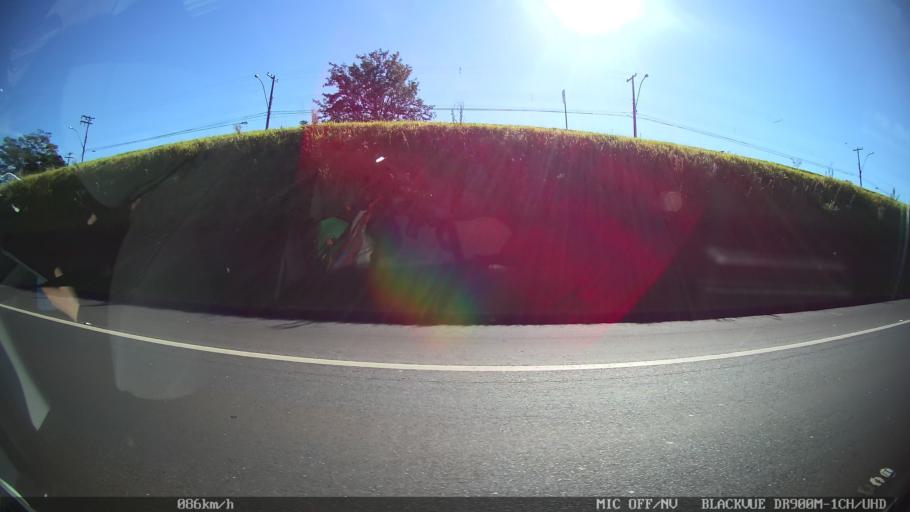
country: BR
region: Sao Paulo
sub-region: Franca
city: Franca
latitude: -20.5686
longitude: -47.4039
